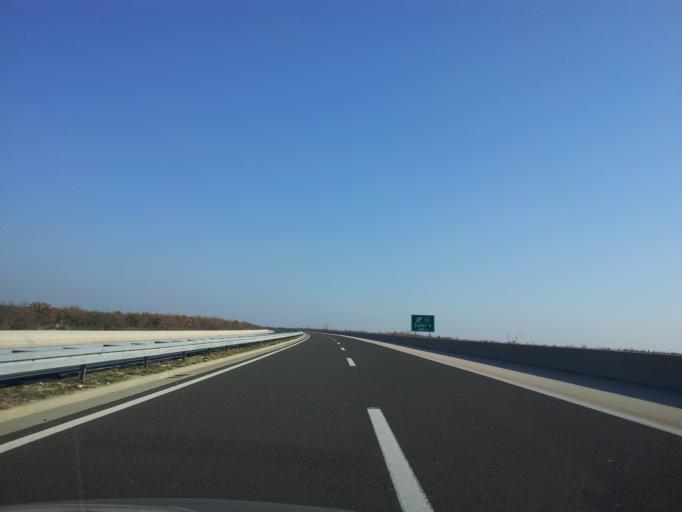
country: HR
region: Zadarska
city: Galovac
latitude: 44.1288
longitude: 15.4245
